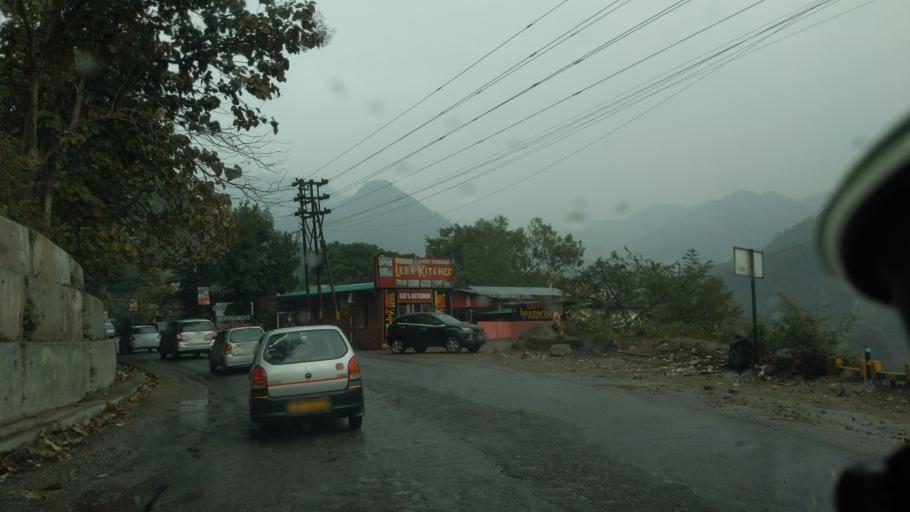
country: IN
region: Uttarakhand
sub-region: Naini Tal
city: Haldwani
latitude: 29.2803
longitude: 79.5451
